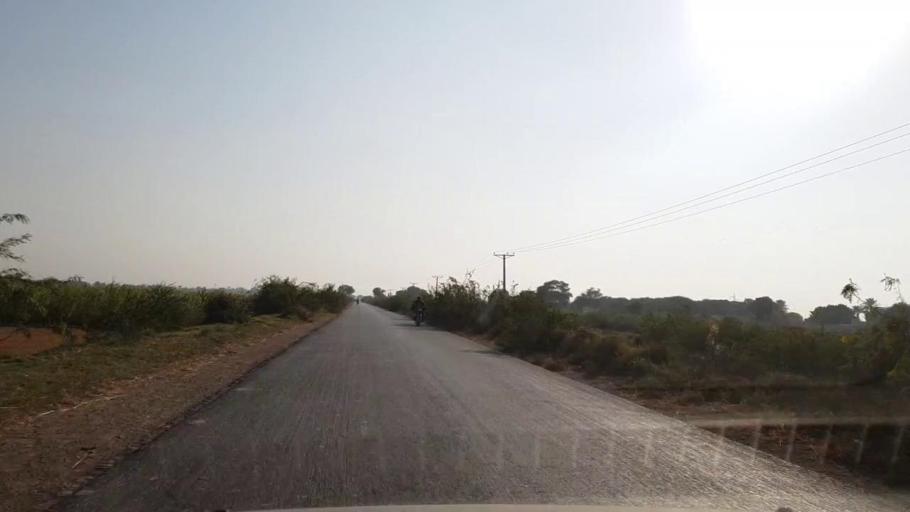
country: PK
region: Sindh
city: Bulri
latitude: 24.8880
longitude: 68.3431
